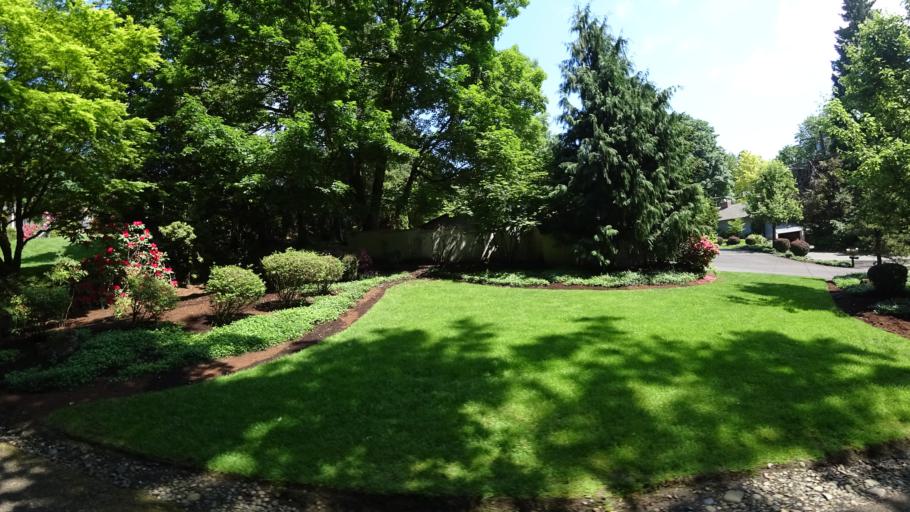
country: US
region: Oregon
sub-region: Washington County
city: West Haven-Sylvan
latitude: 45.5197
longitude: -122.7250
